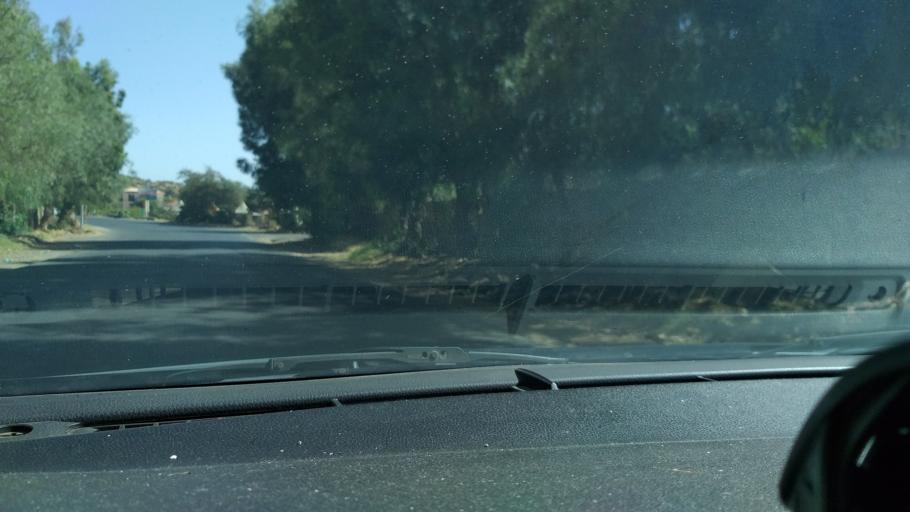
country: SA
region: Makkah
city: Ash Shafa
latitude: 21.0770
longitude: 40.3265
